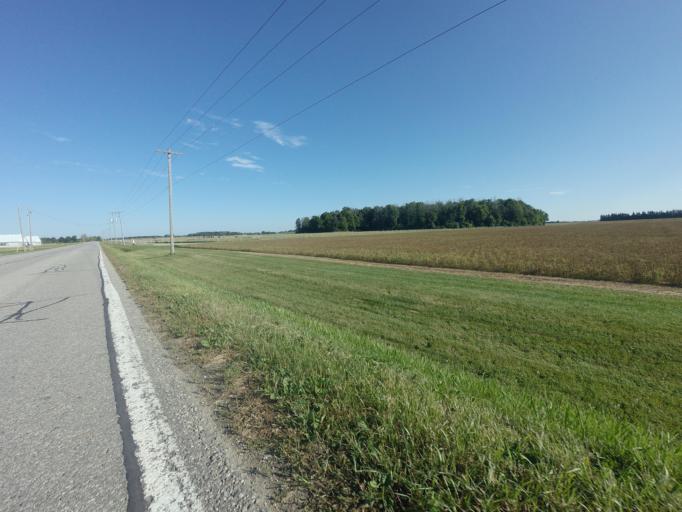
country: CA
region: Ontario
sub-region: Wellington County
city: Guelph
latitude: 43.6448
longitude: -80.4078
